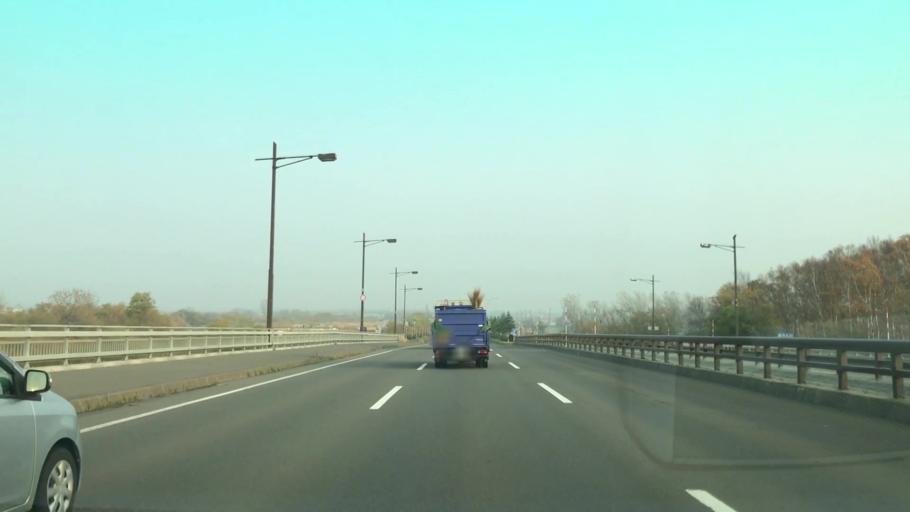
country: JP
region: Hokkaido
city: Ishikari
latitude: 43.1684
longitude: 141.3485
